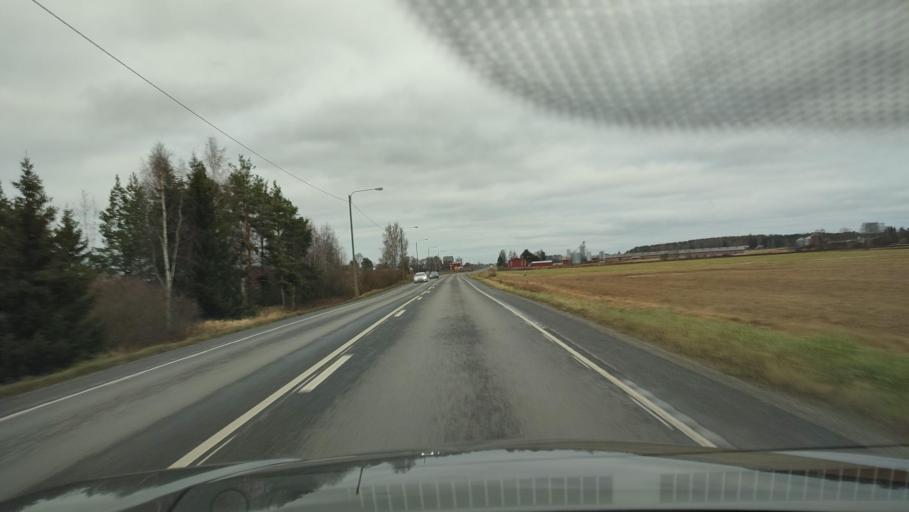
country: FI
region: Southern Ostrobothnia
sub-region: Seinaejoki
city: Ilmajoki
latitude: 62.7036
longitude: 22.5210
